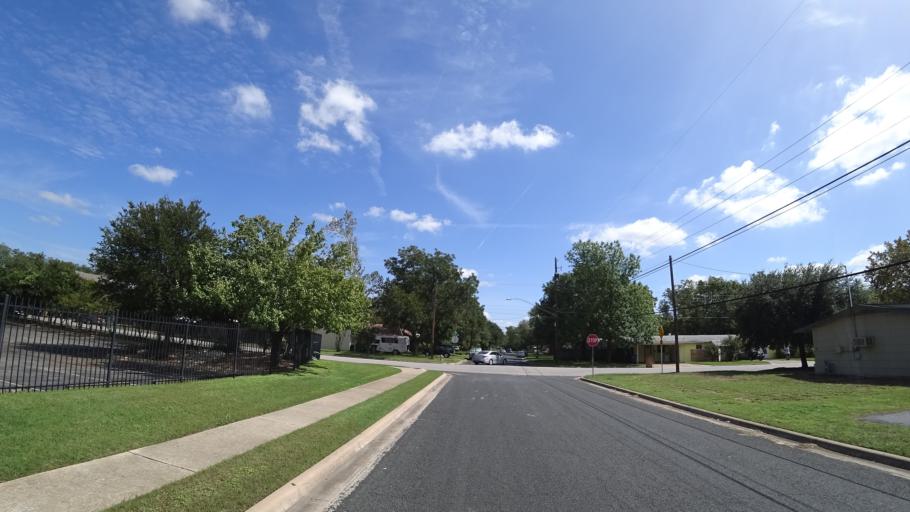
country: US
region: Texas
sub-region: Travis County
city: Austin
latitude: 30.3453
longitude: -97.7337
